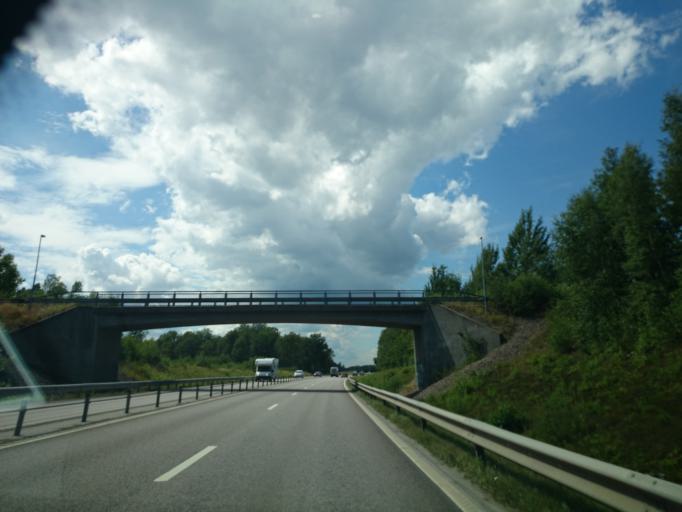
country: SE
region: Kalmar
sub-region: Kalmar Kommun
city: Rinkabyholm
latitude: 56.6640
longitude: 16.2654
